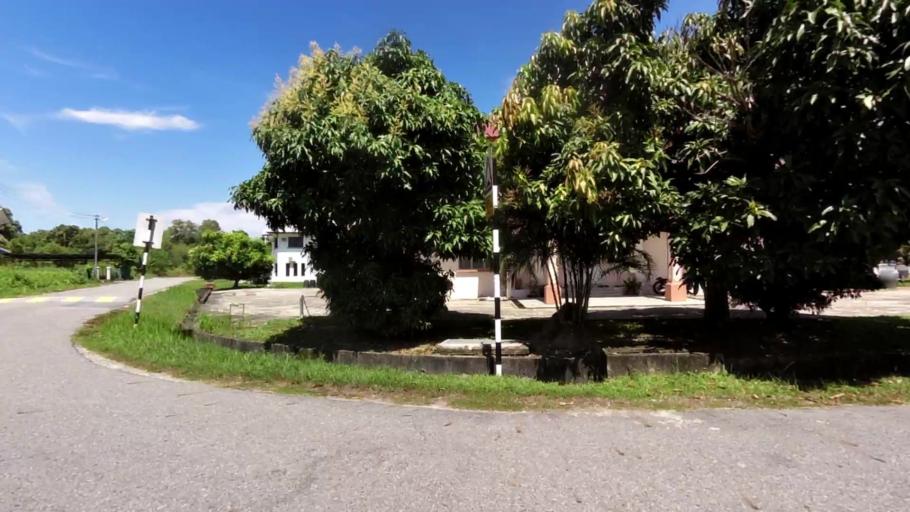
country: BN
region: Brunei and Muara
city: Bandar Seri Begawan
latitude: 4.9386
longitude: 114.9456
